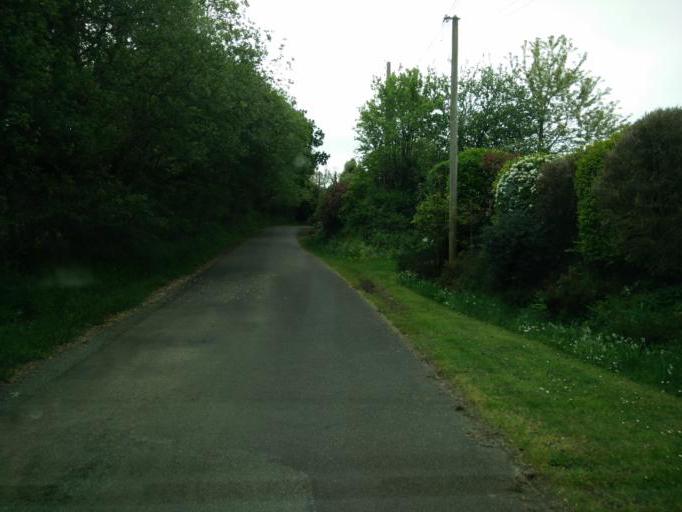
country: FR
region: Brittany
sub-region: Departement du Finistere
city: Tregunc
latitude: 47.8288
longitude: -3.8769
